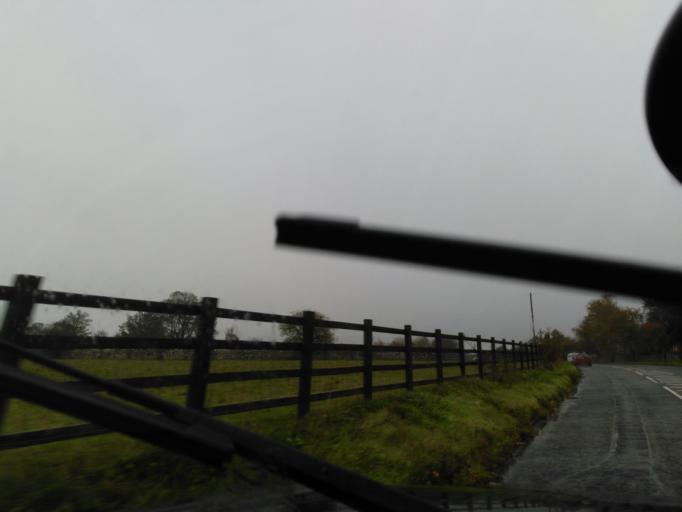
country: GB
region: England
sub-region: Bath and North East Somerset
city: Freshford
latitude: 51.3479
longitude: -2.2945
